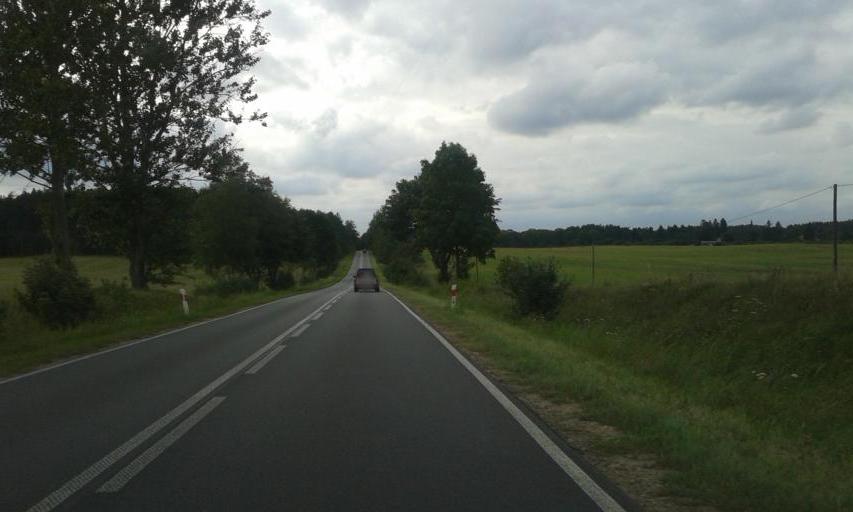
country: PL
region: West Pomeranian Voivodeship
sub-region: Powiat szczecinecki
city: Szczecinek
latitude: 53.7154
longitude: 16.5696
